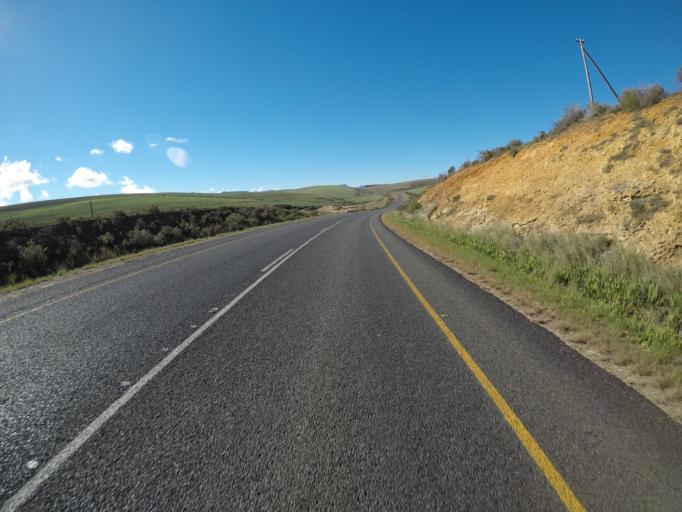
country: ZA
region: Western Cape
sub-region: Overberg District Municipality
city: Caledon
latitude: -34.1516
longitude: 19.4748
